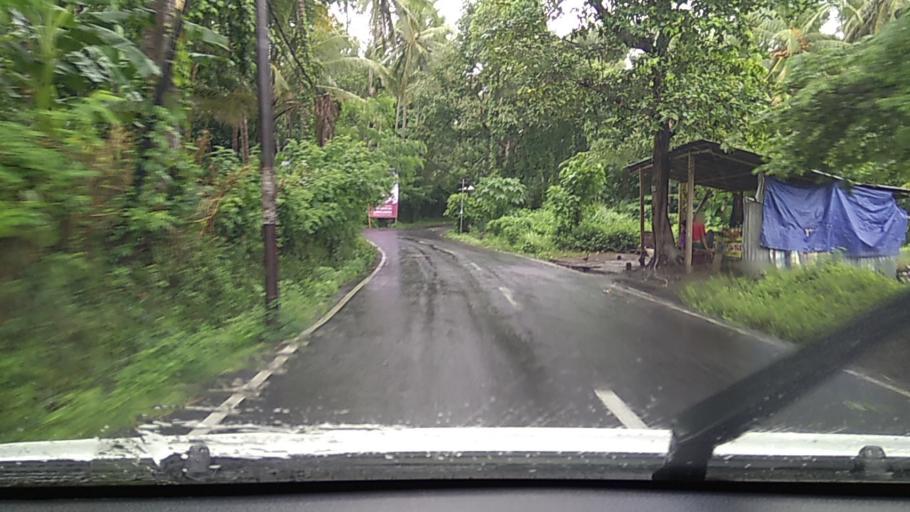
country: ID
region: Bali
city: Banjar Timbrah
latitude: -8.4743
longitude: 115.6183
